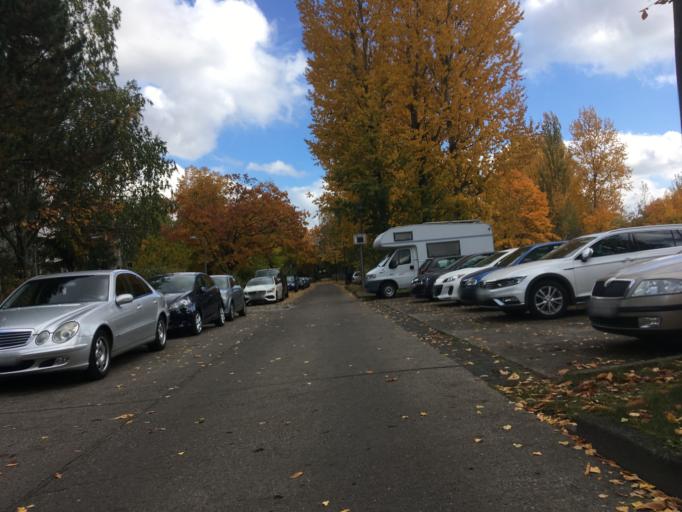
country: DE
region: Berlin
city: Oberschoneweide
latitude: 52.4488
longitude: 13.5292
